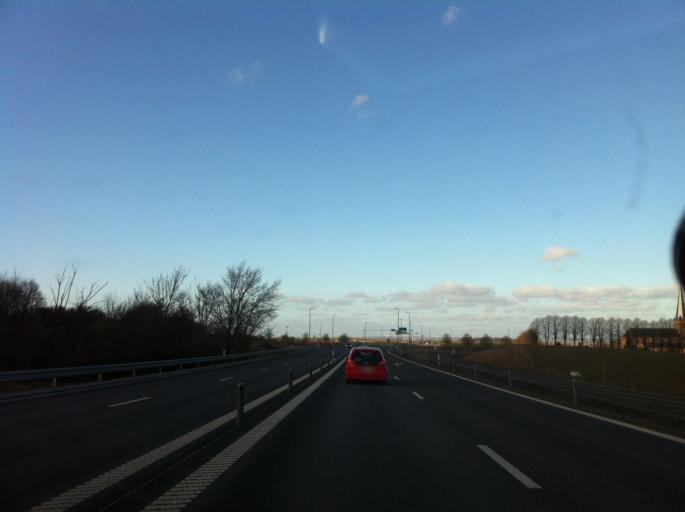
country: SE
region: Skane
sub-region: Svedala Kommun
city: Svedala
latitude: 55.5317
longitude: 13.2656
